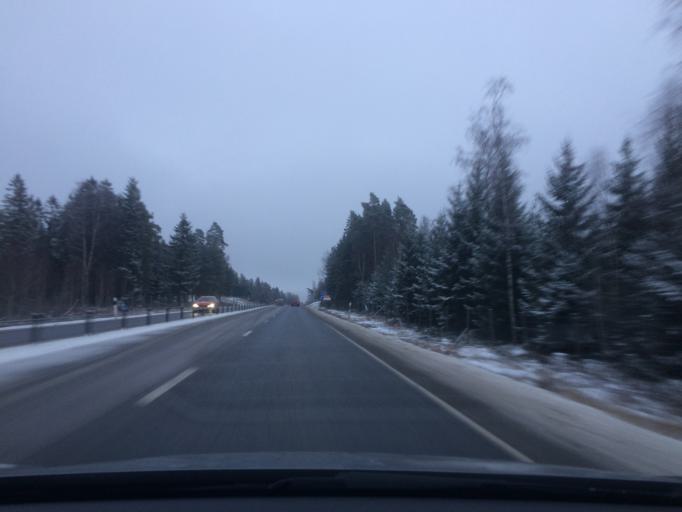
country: SE
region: Kronoberg
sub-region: Vaxjo Kommun
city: Vaexjoe
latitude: 56.8839
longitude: 14.8550
